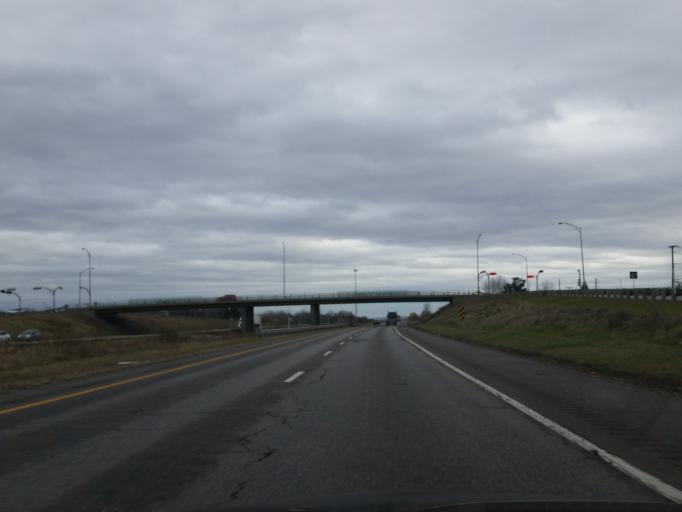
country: CA
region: Quebec
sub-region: Outaouais
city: Gatineau
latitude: 45.5111
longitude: -75.6462
